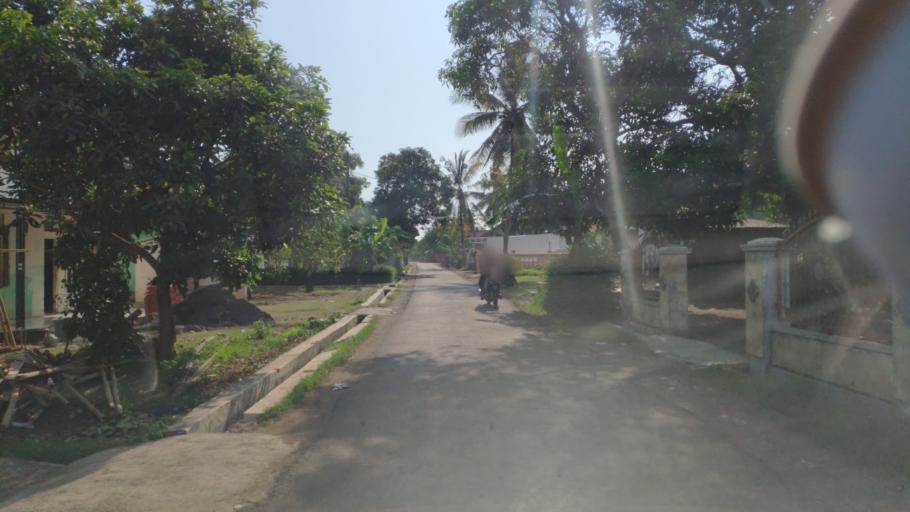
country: ID
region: Central Java
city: Karangbadar Kidul
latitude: -7.7003
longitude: 108.9854
